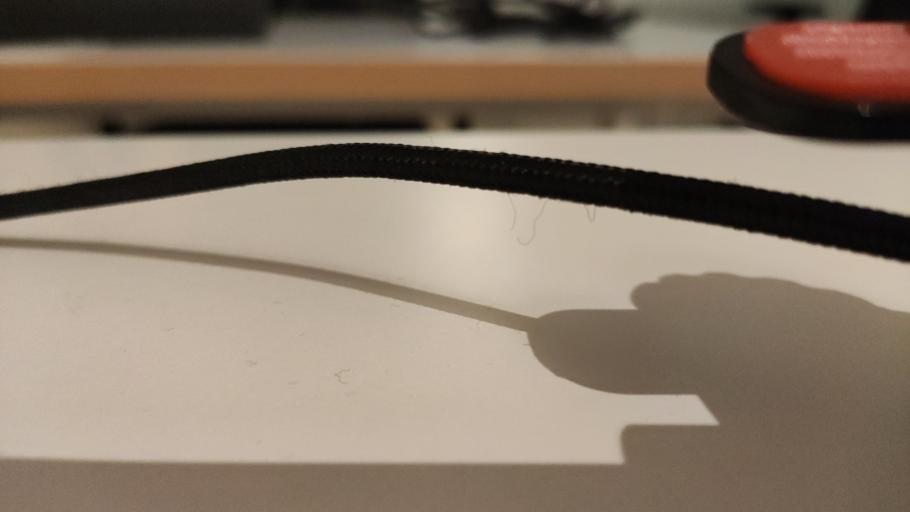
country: RU
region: Moskovskaya
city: Meshcherino
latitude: 55.1435
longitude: 38.2851
